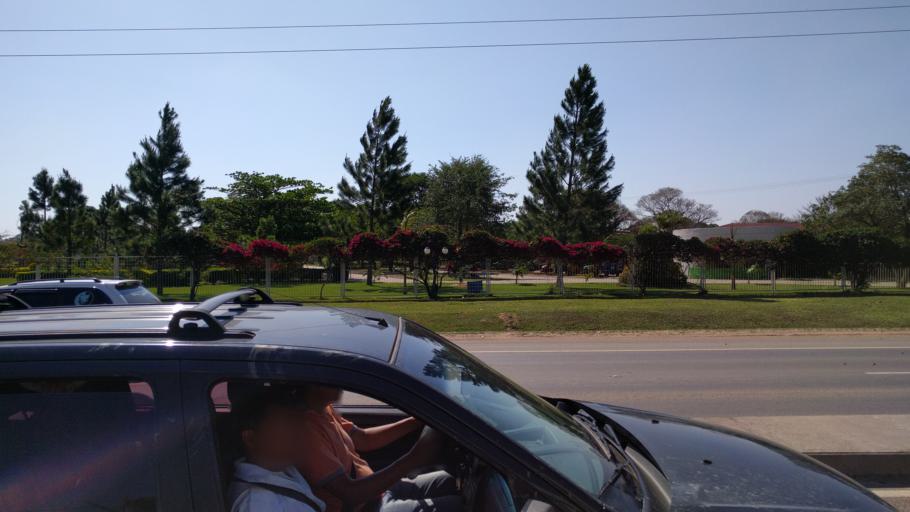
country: BO
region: Santa Cruz
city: Cotoca
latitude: -17.7634
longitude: -63.0296
